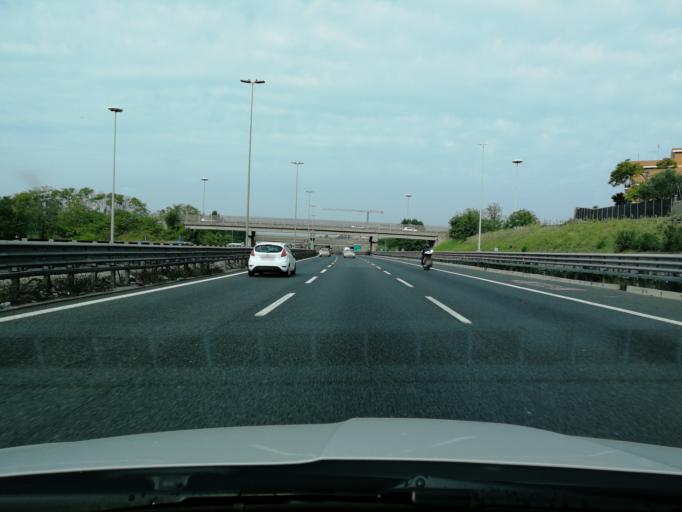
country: IT
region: Latium
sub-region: Citta metropolitana di Roma Capitale
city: Setteville
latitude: 41.8889
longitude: 12.6145
